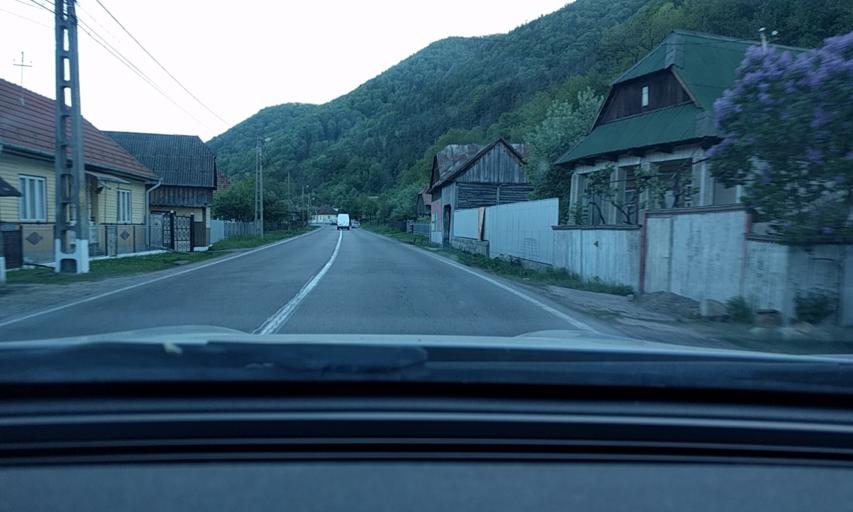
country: RO
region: Bacau
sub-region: Oras Slanic-Moldova
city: Slanic-Moldova
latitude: 46.1649
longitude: 26.4676
